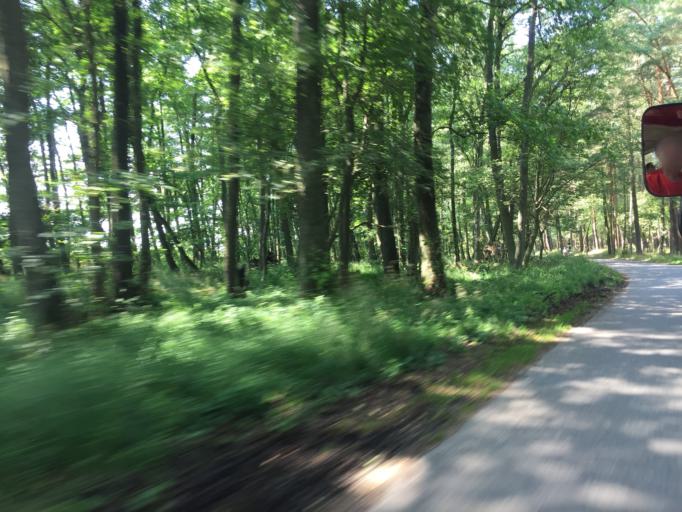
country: PL
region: Pomeranian Voivodeship
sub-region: Powiat leborski
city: Leba
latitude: 54.7524
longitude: 17.4768
